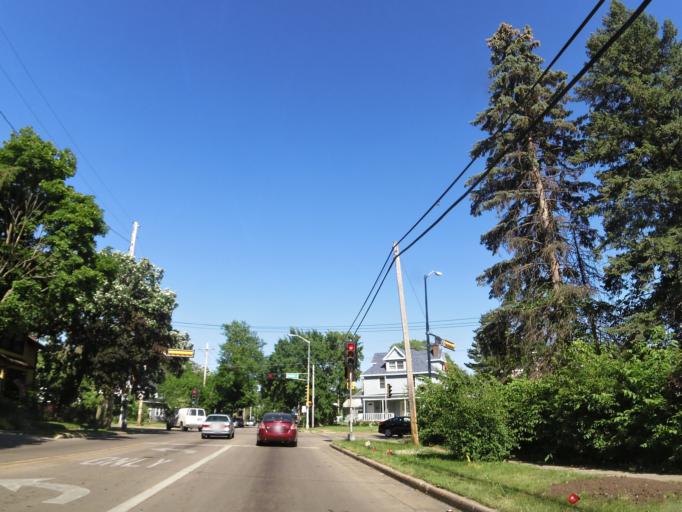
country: US
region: Wisconsin
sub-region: Rock County
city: Beloit
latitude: 42.5110
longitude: -89.0218
